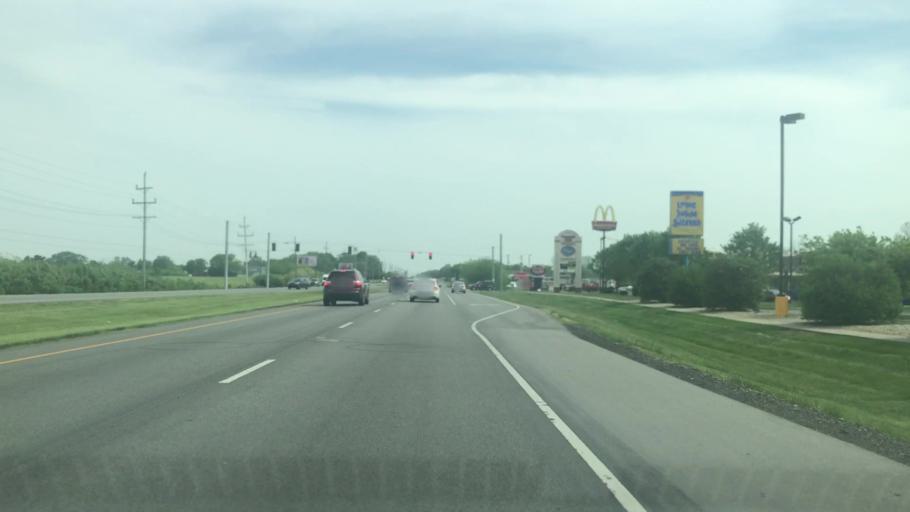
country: US
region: Indiana
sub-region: Johnson County
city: New Whiteland
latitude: 39.5851
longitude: -86.1003
